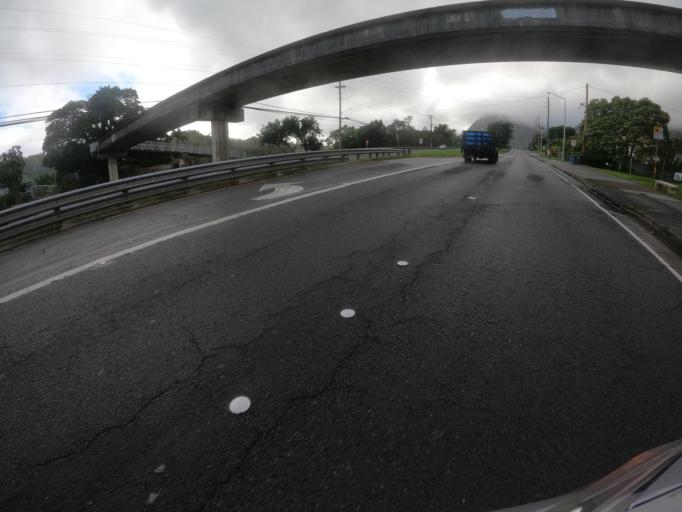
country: US
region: Hawaii
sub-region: Honolulu County
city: Kane'ohe
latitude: 21.3963
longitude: -157.7978
